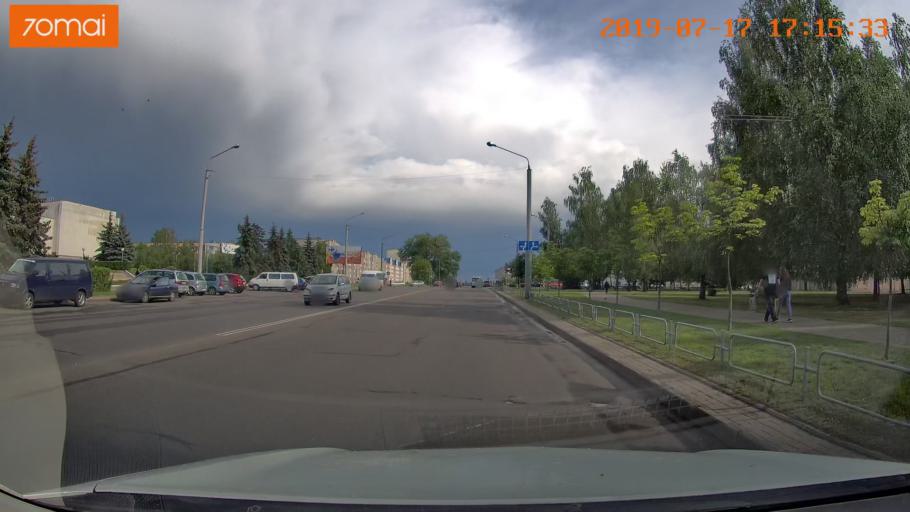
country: BY
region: Mogilev
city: Babruysk
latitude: 53.1691
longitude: 29.1922
